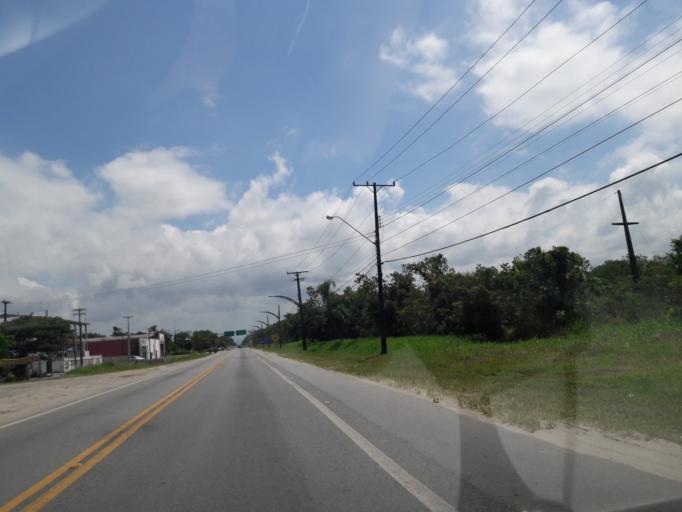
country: BR
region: Parana
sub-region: Pontal Do Parana
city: Pontal do Parana
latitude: -25.6946
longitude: -48.4801
